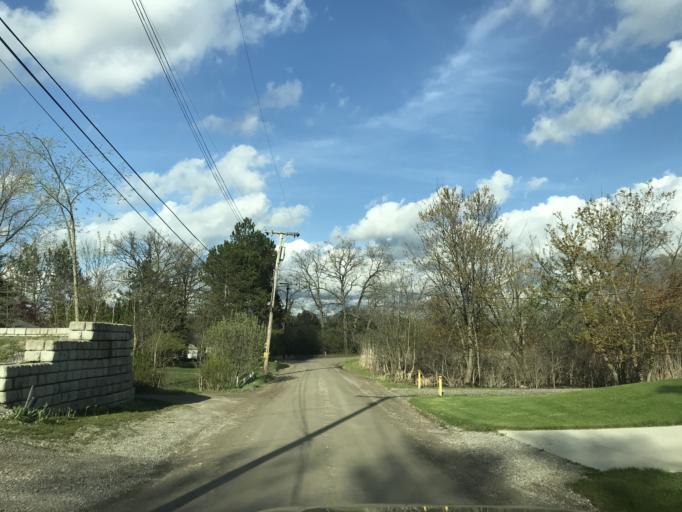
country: US
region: Michigan
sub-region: Livingston County
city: Brighton
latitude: 42.5444
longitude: -83.7543
